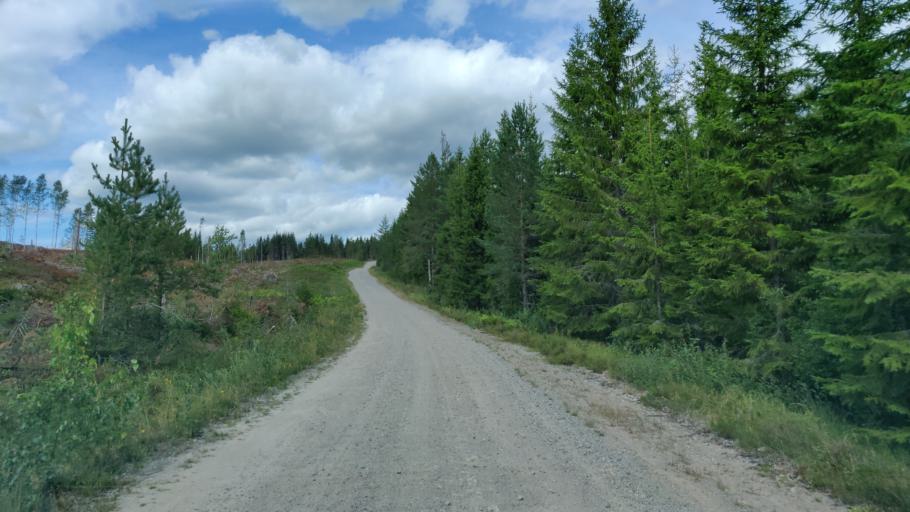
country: SE
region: Vaermland
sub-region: Hagfors Kommun
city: Hagfors
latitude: 60.0174
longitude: 13.7304
